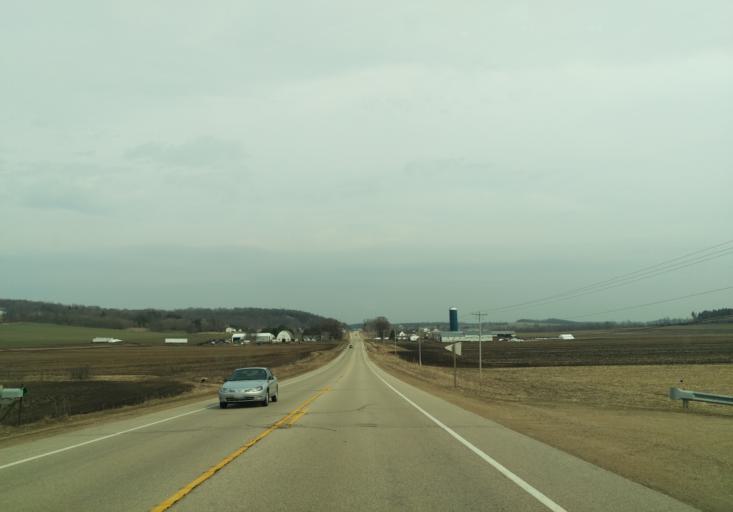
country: US
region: Wisconsin
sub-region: Columbia County
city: Lodi
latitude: 43.2745
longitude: -89.5213
